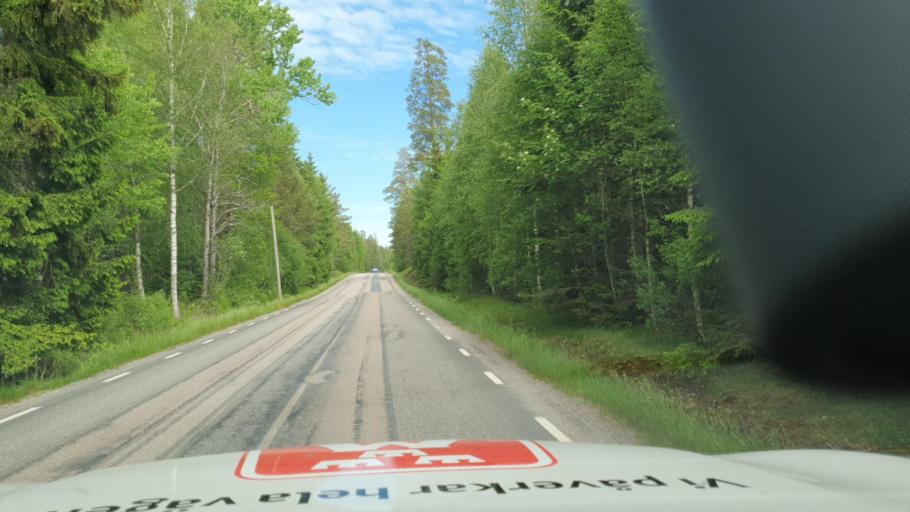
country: SE
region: Vaestra Goetaland
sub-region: Alingsas Kommun
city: Sollebrunn
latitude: 58.2134
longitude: 12.5974
